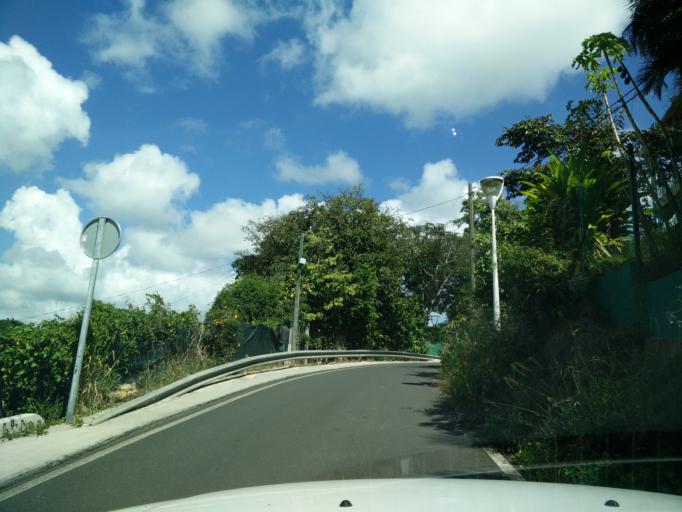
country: GP
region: Guadeloupe
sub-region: Guadeloupe
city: Le Gosier
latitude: 16.2165
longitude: -61.5174
